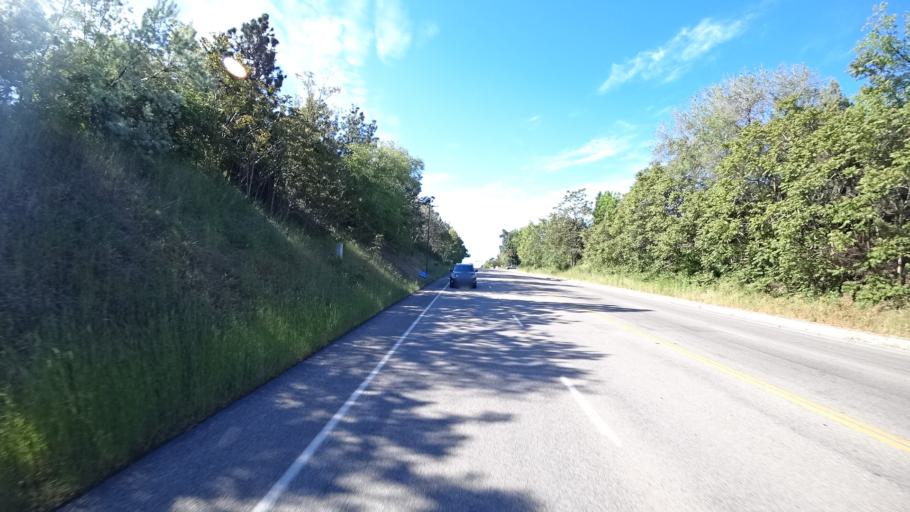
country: US
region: Idaho
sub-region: Ada County
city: Garden City
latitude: 43.5879
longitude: -116.2436
